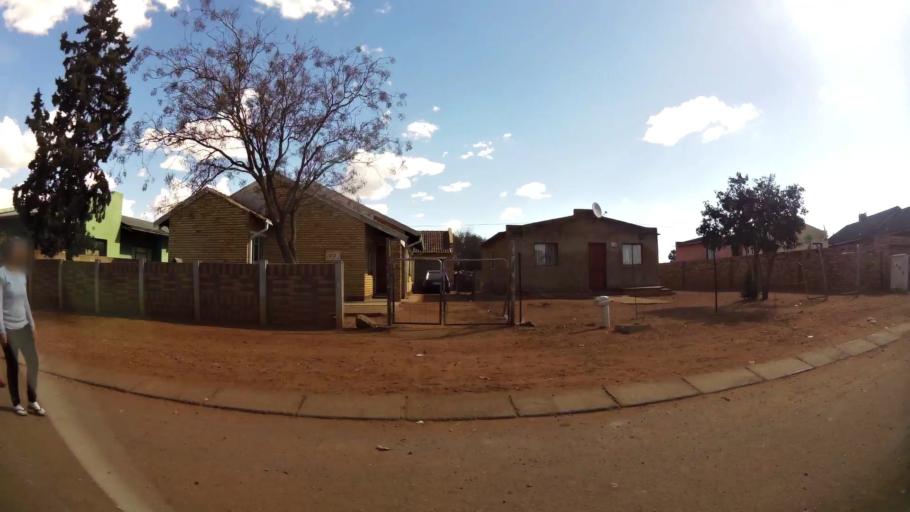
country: ZA
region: North-West
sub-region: Dr Kenneth Kaunda District Municipality
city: Klerksdorp
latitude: -26.8685
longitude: 26.5819
